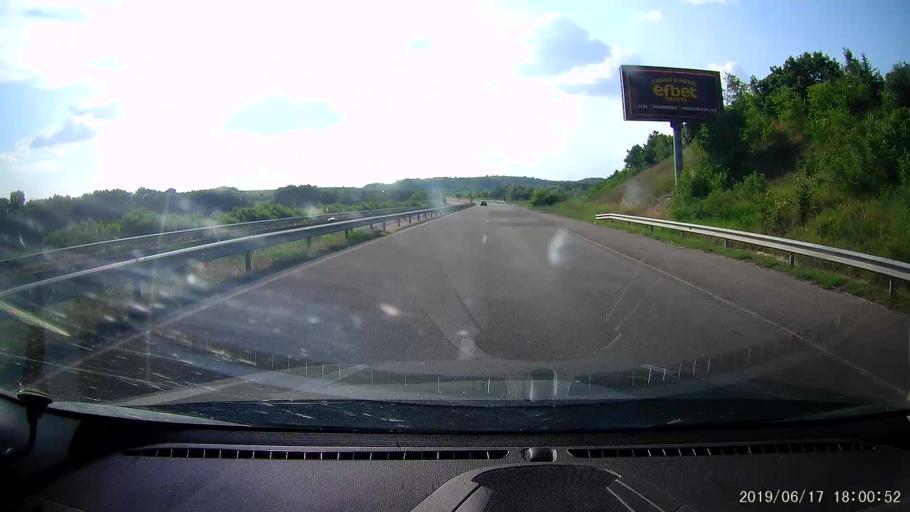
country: BG
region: Khaskovo
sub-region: Obshtina Svilengrad
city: Svilengrad
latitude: 41.7413
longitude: 26.2703
